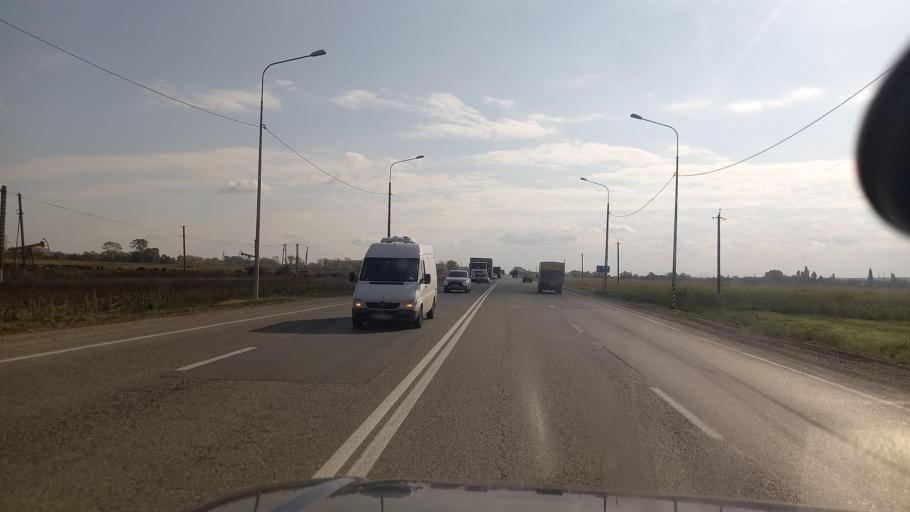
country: RU
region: Krasnodarskiy
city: Novoukrainskiy
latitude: 44.8932
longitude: 38.0651
